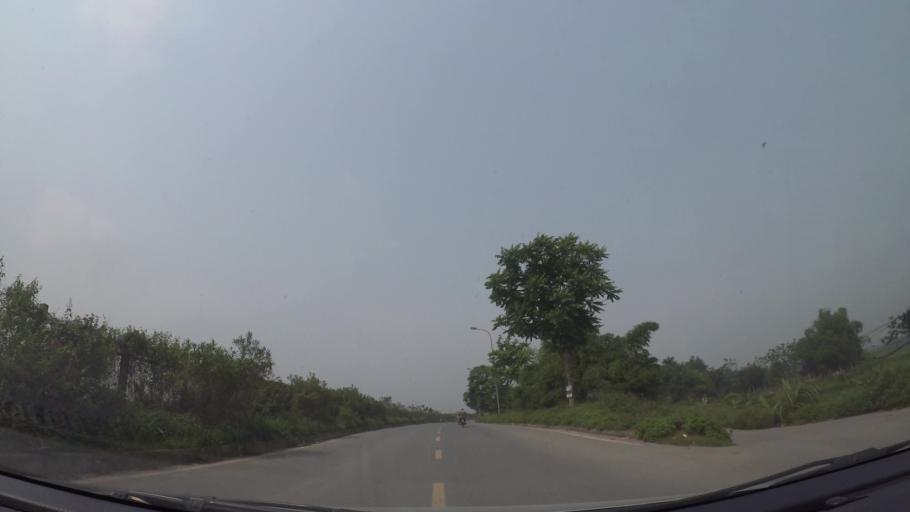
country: VN
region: Ha Noi
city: Quoc Oai
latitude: 20.9979
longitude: 105.5933
